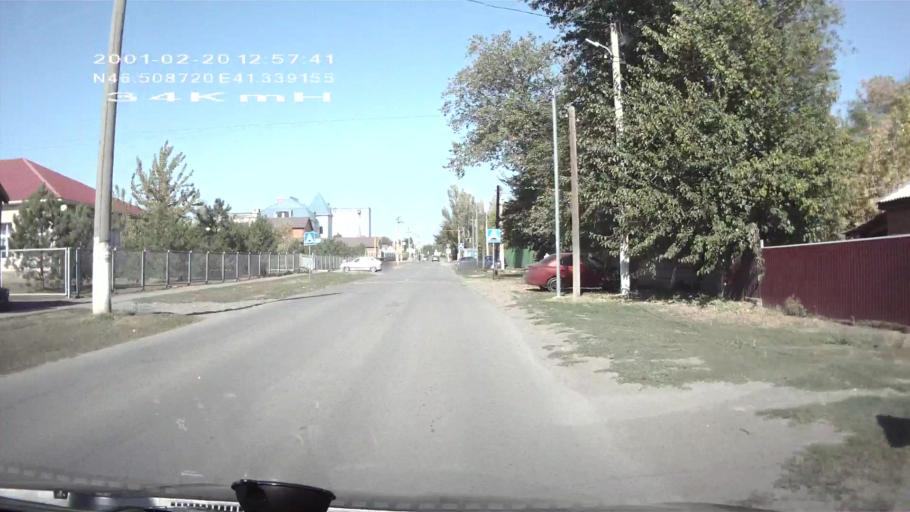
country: RU
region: Rostov
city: Gigant
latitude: 46.5088
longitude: 41.3392
